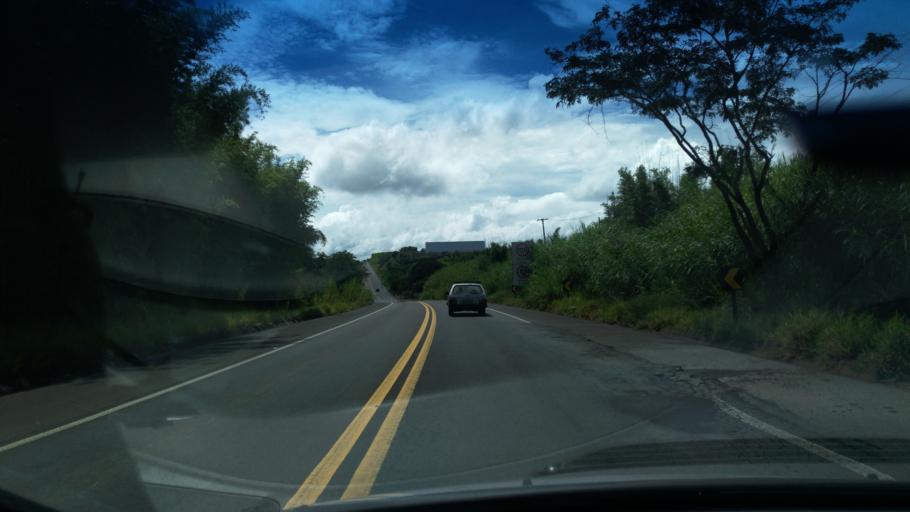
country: BR
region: Sao Paulo
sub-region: Santo Antonio Do Jardim
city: Espirito Santo do Pinhal
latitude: -22.1605
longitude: -46.7301
